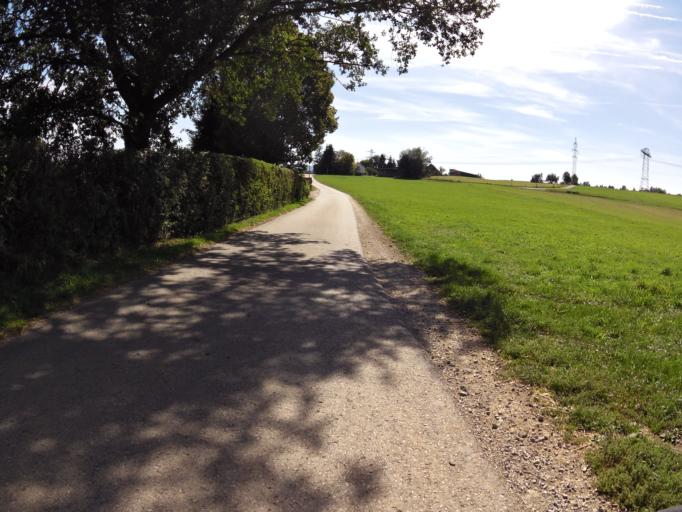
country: DE
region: Baden-Wuerttemberg
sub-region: Freiburg Region
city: Donaueschingen
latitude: 47.9720
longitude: 8.5051
